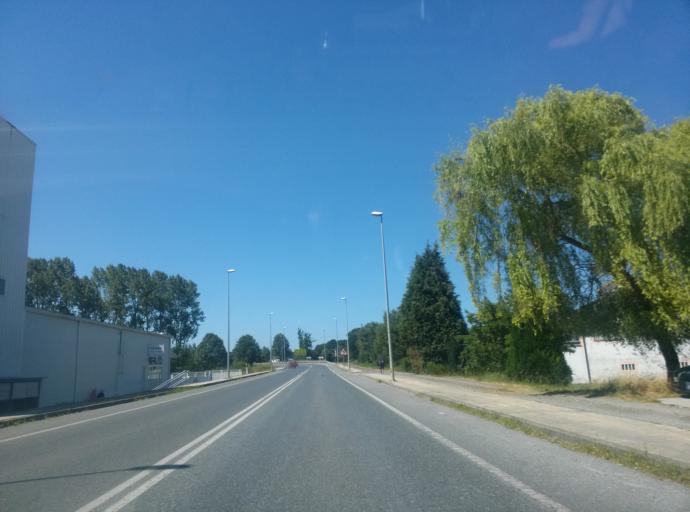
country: ES
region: Galicia
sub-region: Provincia de Lugo
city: Mos
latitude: 43.1344
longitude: -7.4895
